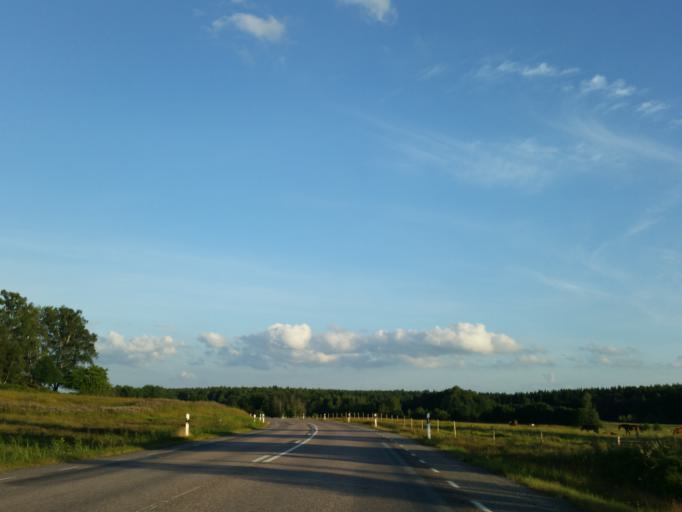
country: SE
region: Stockholm
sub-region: Sodertalje Kommun
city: Soedertaelje
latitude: 59.2243
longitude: 17.5635
